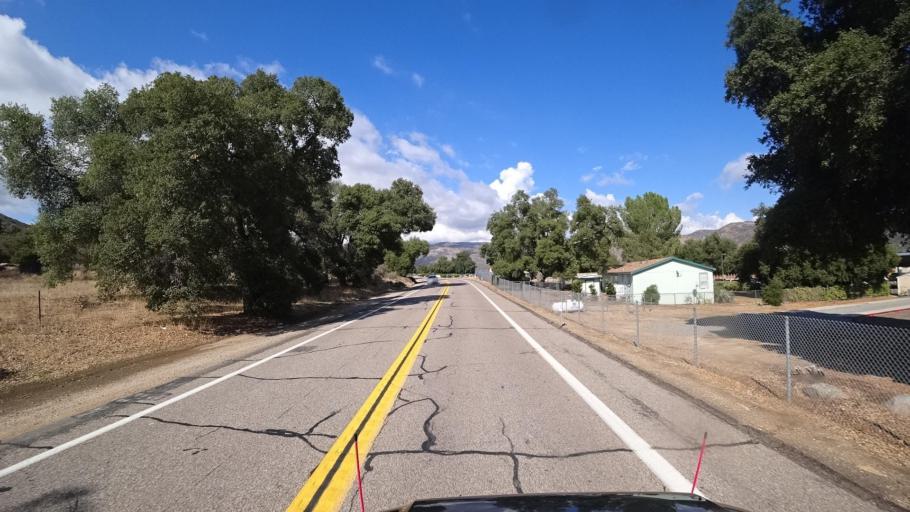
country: US
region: California
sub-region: San Diego County
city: Pine Valley
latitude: 32.7321
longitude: -116.4943
